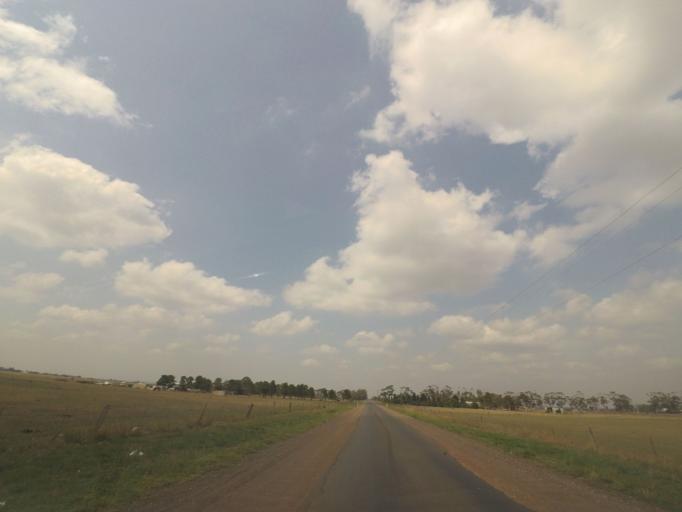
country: AU
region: Victoria
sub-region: Melton
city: Melton West
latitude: -37.6520
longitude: 144.5560
